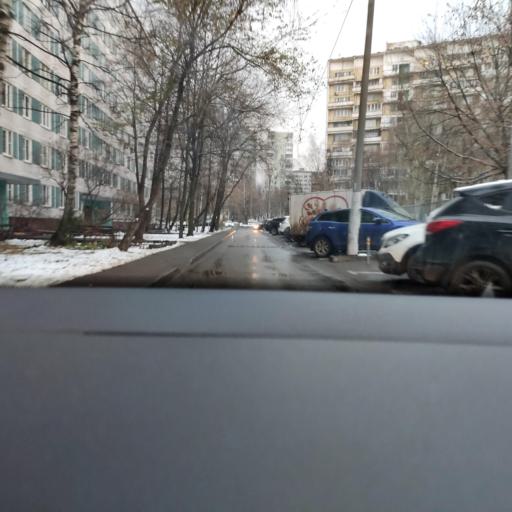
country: RU
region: Moscow
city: Bibirevo
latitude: 55.8907
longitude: 37.6128
